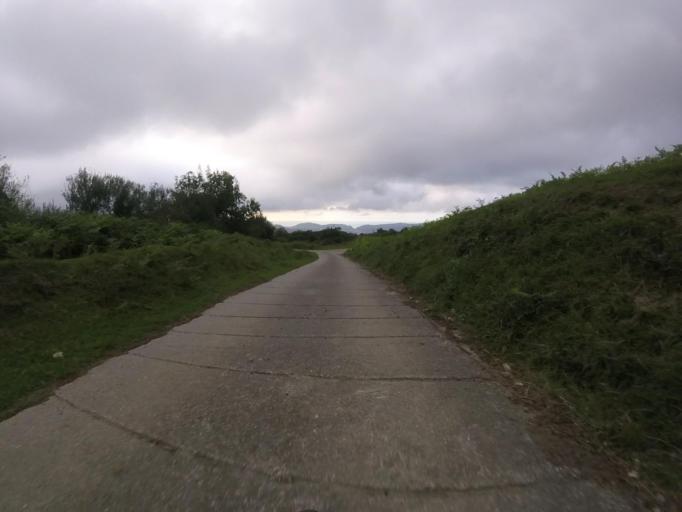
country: ES
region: Basque Country
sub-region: Provincia de Guipuzcoa
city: Irun
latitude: 43.2630
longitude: -1.8295
